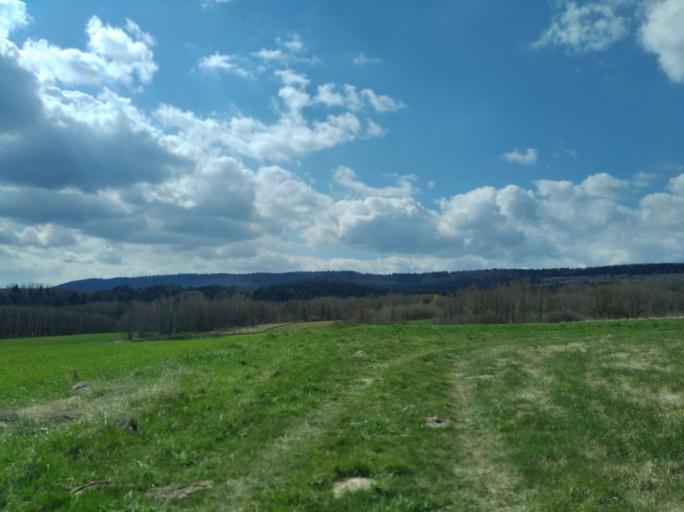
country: PL
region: Subcarpathian Voivodeship
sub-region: Powiat strzyzowski
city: Strzyzow
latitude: 49.8460
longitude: 21.7895
